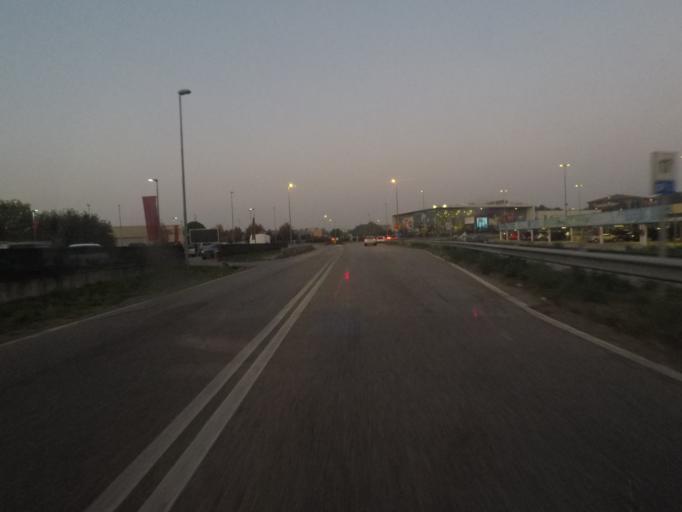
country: IT
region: Lombardy
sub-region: Provincia di Monza e Brianza
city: Concorezzo
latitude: 45.5820
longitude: 9.3265
